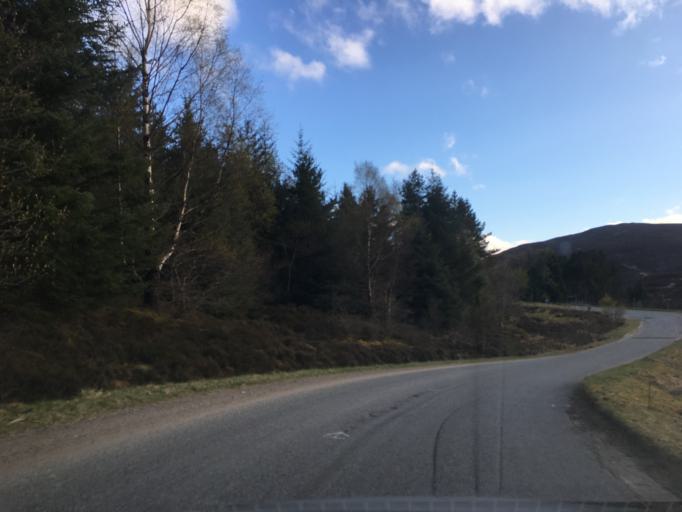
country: GB
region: Scotland
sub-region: Perth and Kinross
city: Aberfeldy
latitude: 56.6676
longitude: -3.9947
